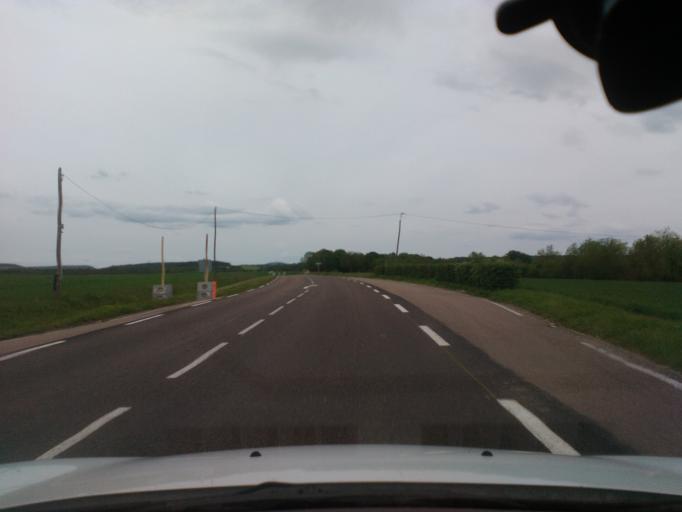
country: FR
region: Champagne-Ardenne
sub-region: Departement de l'Aube
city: Bar-sur-Aube
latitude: 48.2242
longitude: 4.7355
